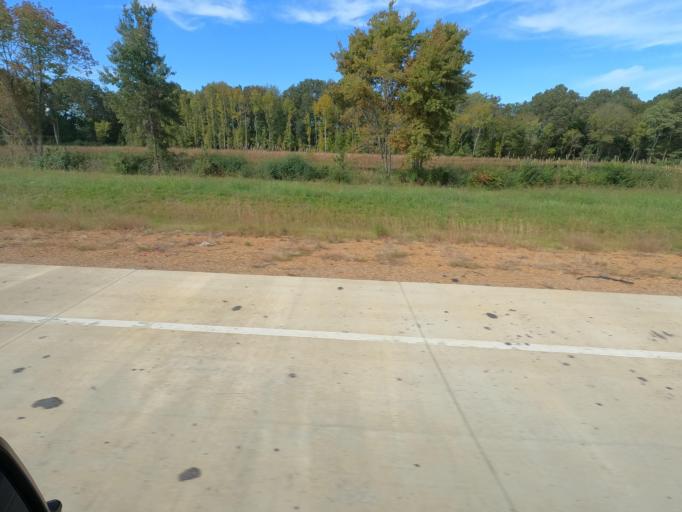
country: US
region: Tennessee
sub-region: Shelby County
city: Arlington
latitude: 35.2881
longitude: -89.6161
